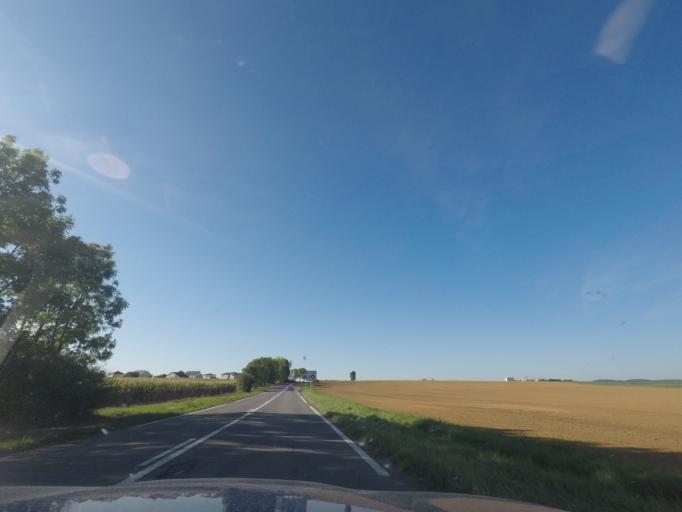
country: LU
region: Luxembourg
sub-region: Canton d'Esch-sur-Alzette
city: Frisange
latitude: 49.4659
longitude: 6.1834
